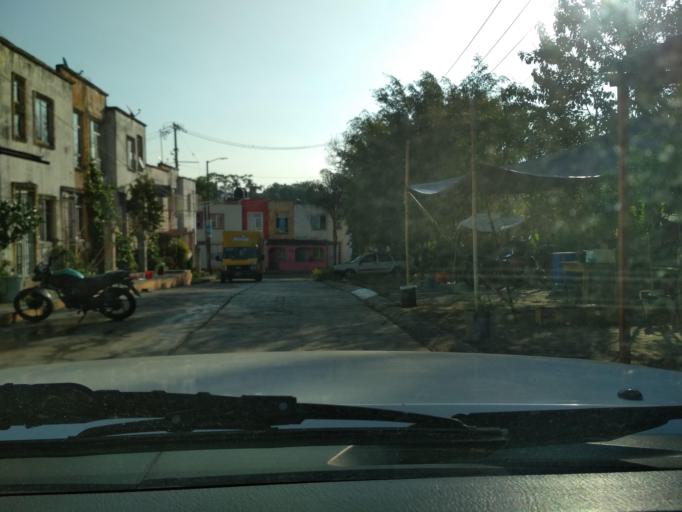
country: MX
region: Veracruz
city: Cordoba
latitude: 18.8686
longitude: -96.9334
